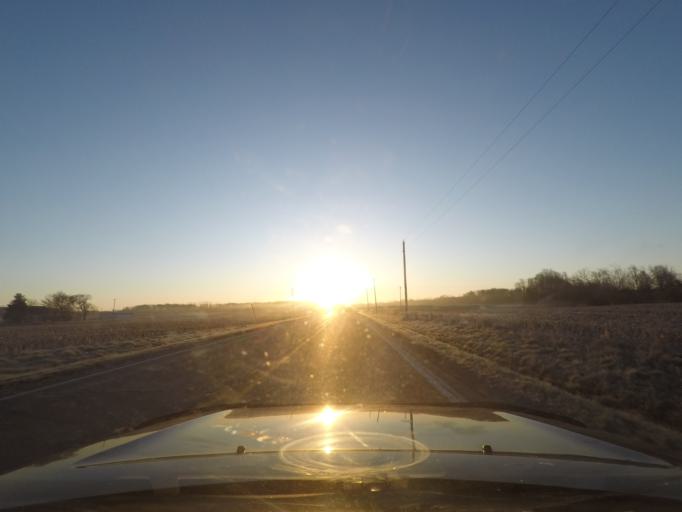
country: US
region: Indiana
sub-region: Marshall County
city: Plymouth
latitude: 41.4488
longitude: -86.3504
